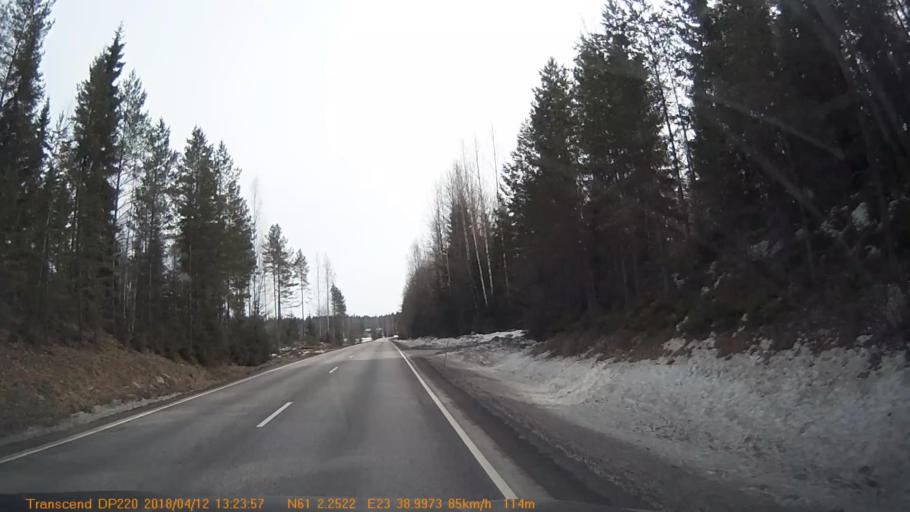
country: FI
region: Pirkanmaa
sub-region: Etelae-Pirkanmaa
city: Kylmaekoski
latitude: 61.0365
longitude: 23.6516
